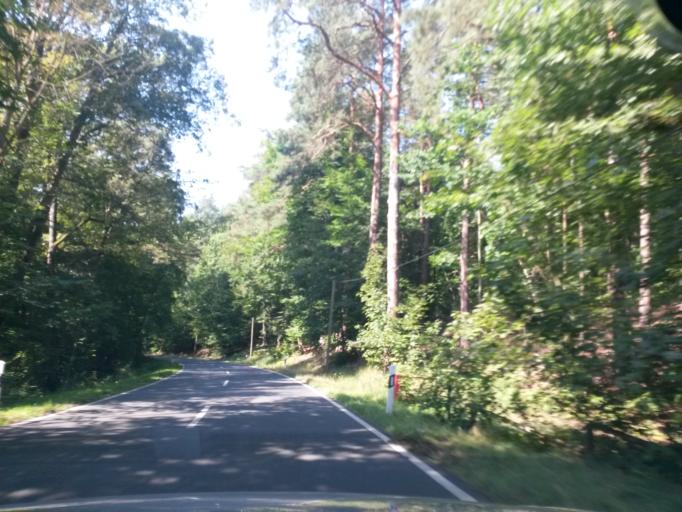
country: DE
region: Brandenburg
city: Joachimsthal
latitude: 52.9560
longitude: 13.7256
